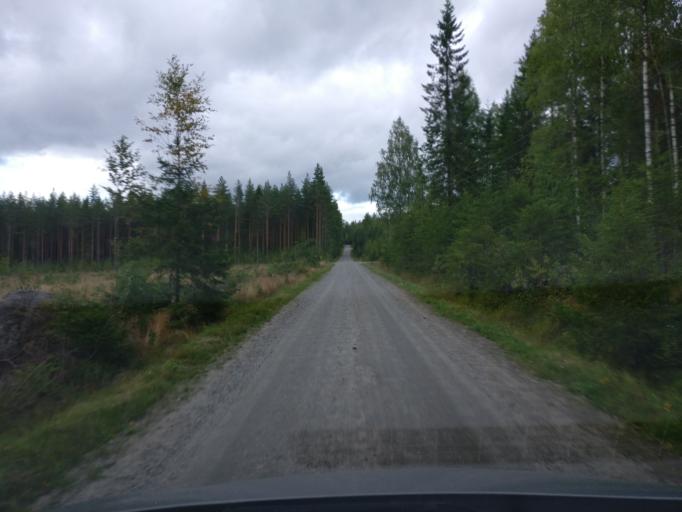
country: FI
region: Central Finland
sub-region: Jyvaeskylae
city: Toivakka
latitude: 62.2110
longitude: 26.1791
